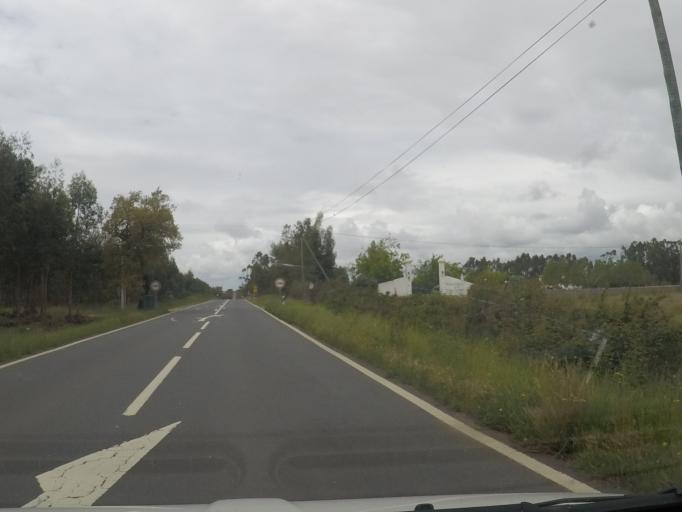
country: PT
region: Setubal
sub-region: Santiago do Cacem
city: Cercal
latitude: 37.8536
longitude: -8.7121
